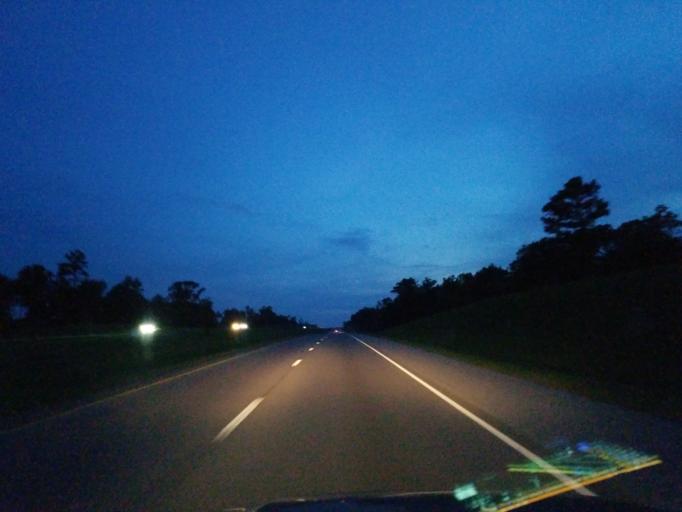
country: US
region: Mississippi
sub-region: Jones County
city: Ellisville
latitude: 31.5647
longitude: -89.2543
